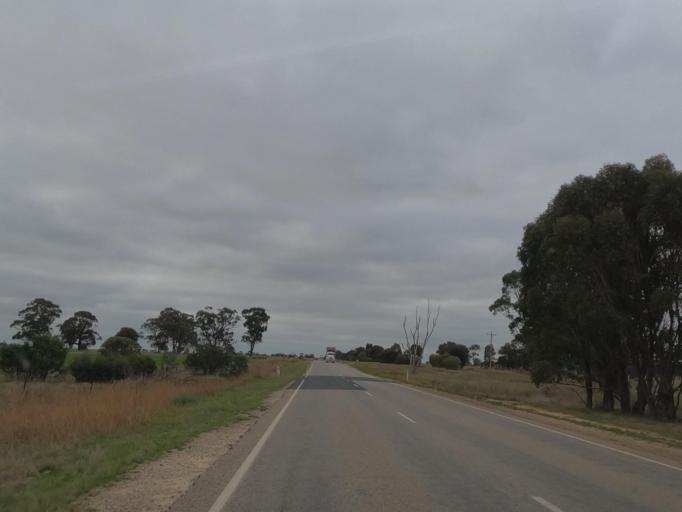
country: AU
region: Victoria
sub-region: Greater Bendigo
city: Long Gully
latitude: -36.5455
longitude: 143.9396
